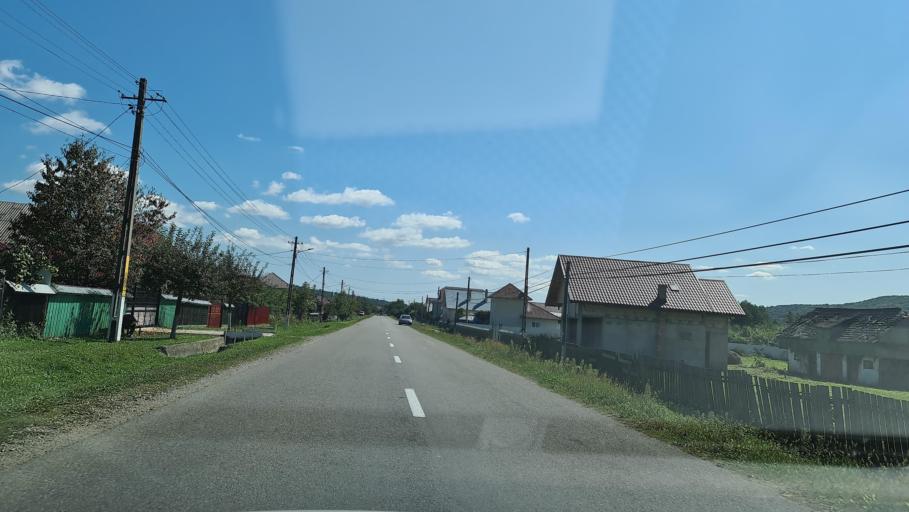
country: RO
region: Bacau
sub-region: Comuna Balcani
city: Frumoasa
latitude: 46.6522
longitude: 26.5573
